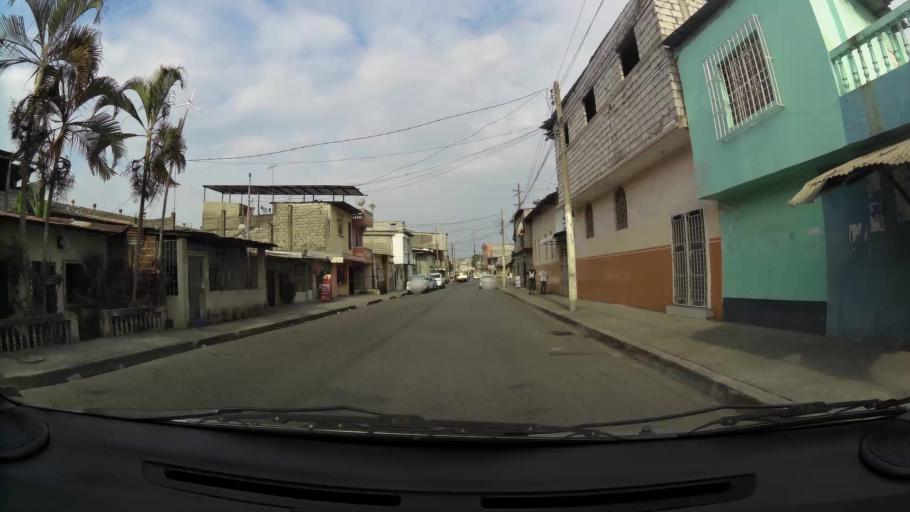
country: EC
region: Guayas
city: Guayaquil
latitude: -2.2501
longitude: -79.9066
